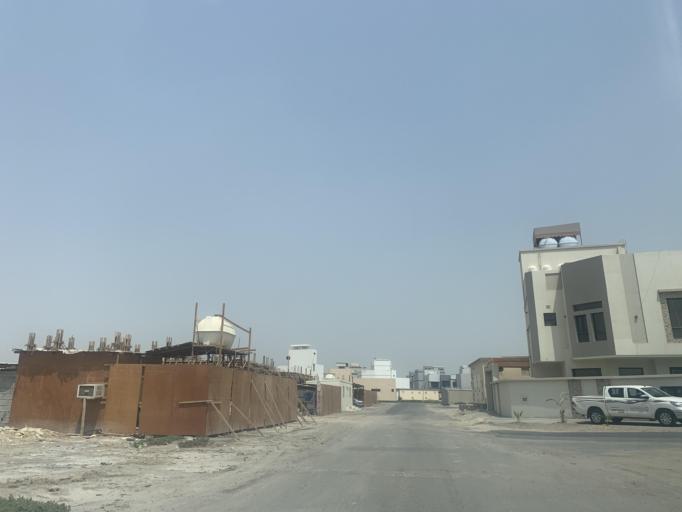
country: BH
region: Central Governorate
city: Madinat Hamad
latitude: 26.1305
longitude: 50.4694
